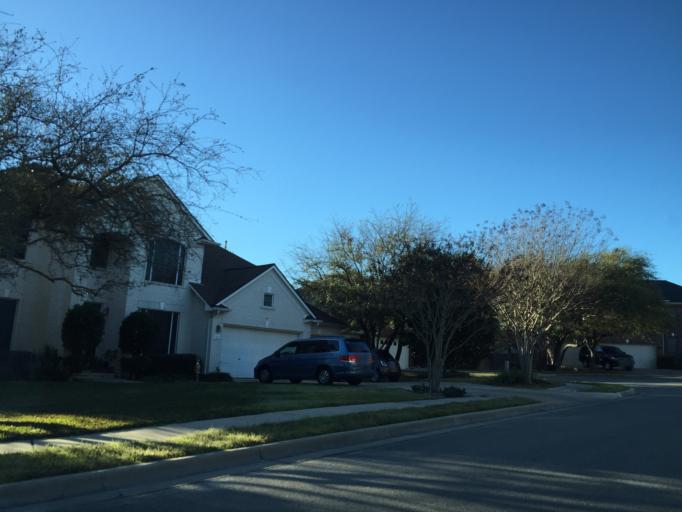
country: US
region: Texas
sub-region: Williamson County
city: Jollyville
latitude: 30.4350
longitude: -97.7841
